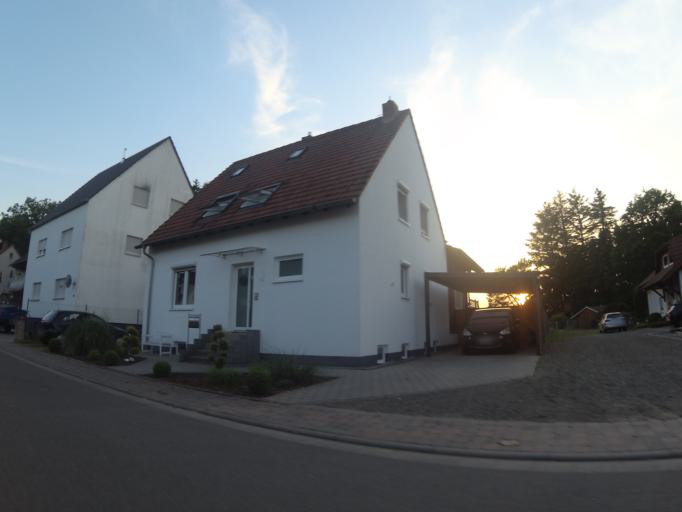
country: DE
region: Rheinland-Pfalz
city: Bruchmuhlbach-Miesau
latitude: 49.4012
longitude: 7.4257
